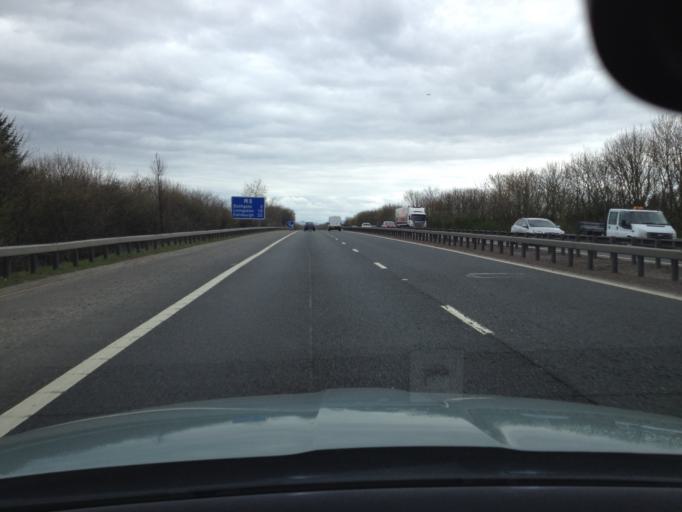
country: GB
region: Scotland
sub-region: West Lothian
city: Whitburn
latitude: 55.8706
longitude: -3.6879
